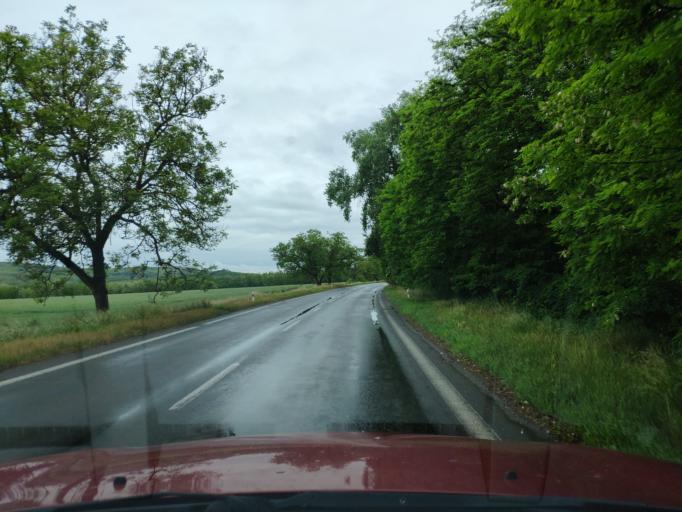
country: HU
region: Borsod-Abauj-Zemplen
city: Karcsa
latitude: 48.3928
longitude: 21.7982
